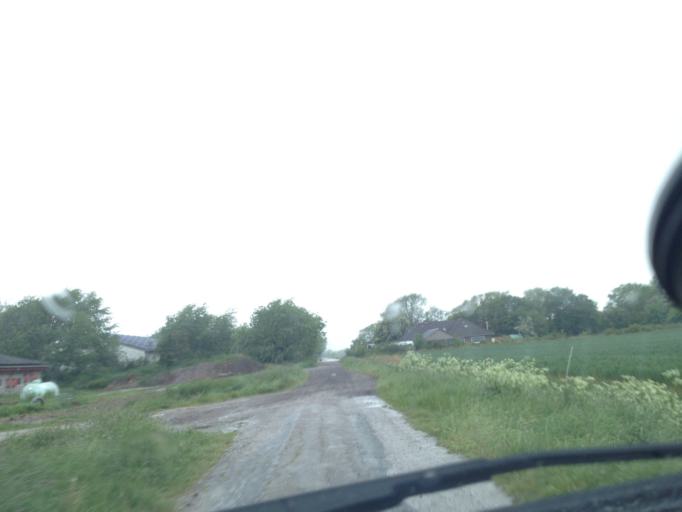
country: DE
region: Schleswig-Holstein
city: Klanxbull
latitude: 54.8864
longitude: 8.6912
